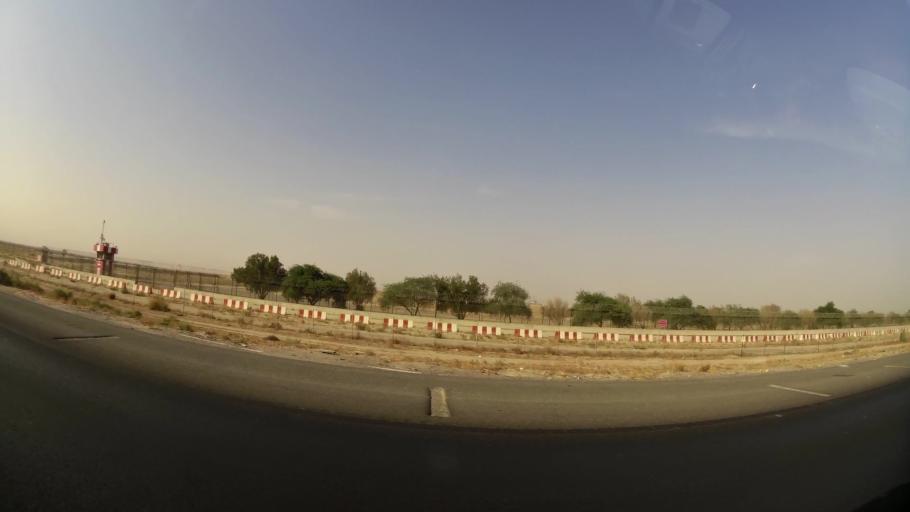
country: KW
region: Al Farwaniyah
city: Janub as Surrah
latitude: 29.2059
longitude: 48.0061
